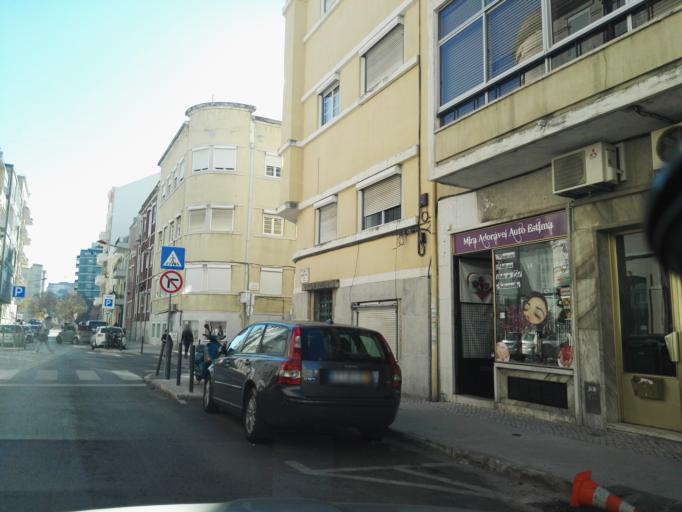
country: PT
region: Lisbon
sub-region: Lisbon
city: Lisbon
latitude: 38.7387
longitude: -9.1311
